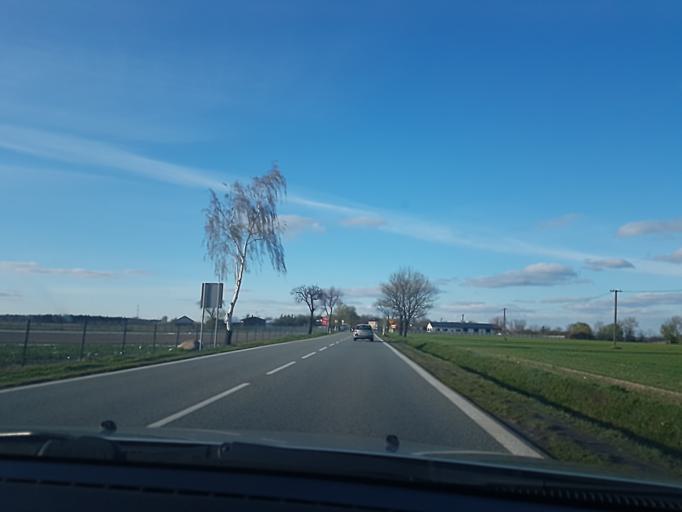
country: PL
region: Lodz Voivodeship
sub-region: Powiat kutnowski
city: Strzelce
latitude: 52.2719
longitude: 19.3913
